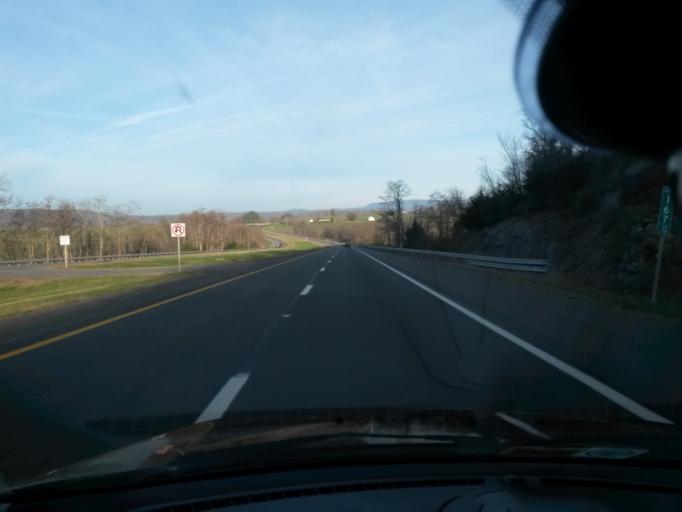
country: US
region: West Virginia
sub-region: Greenbrier County
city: Lewisburg
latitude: 37.8373
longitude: -80.4617
